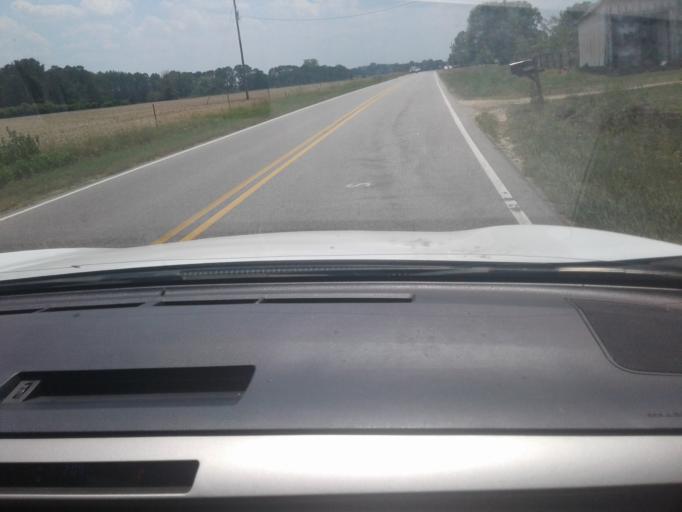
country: US
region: North Carolina
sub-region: Harnett County
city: Coats
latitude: 35.3747
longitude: -78.6259
